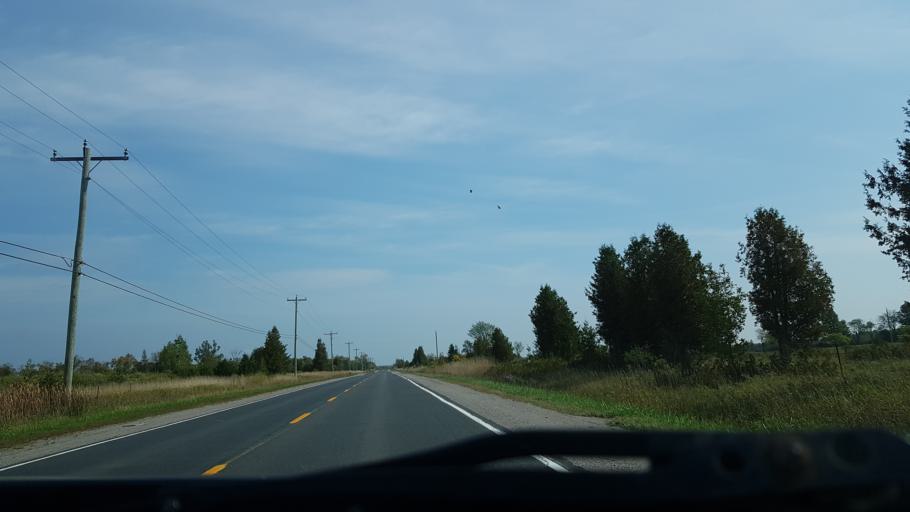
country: CA
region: Ontario
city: Orillia
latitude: 44.6422
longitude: -79.1584
